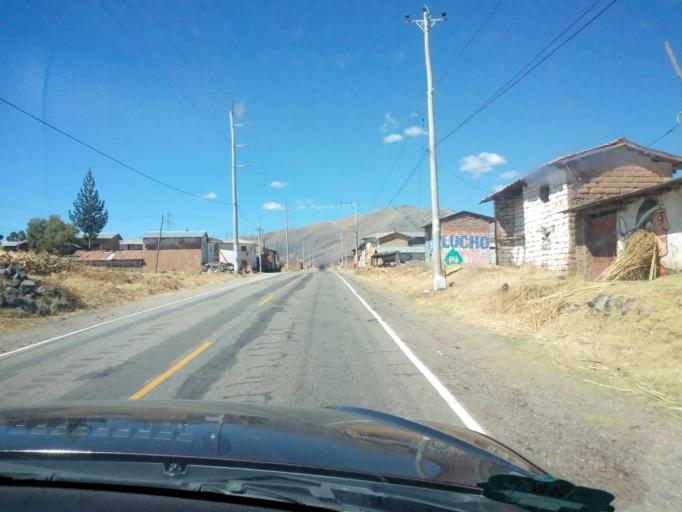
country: PE
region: Cusco
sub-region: Provincia de Canchis
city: Tinta
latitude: -14.1566
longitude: -71.3894
